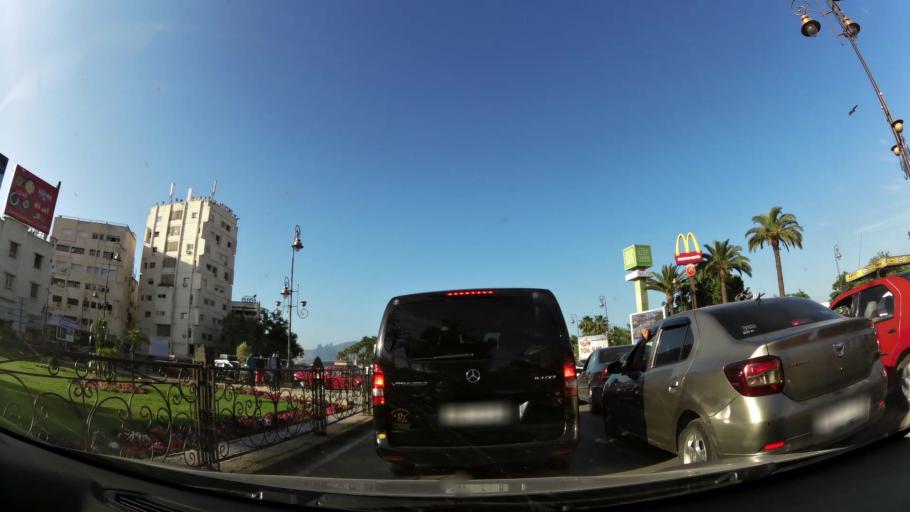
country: MA
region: Fes-Boulemane
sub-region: Fes
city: Fes
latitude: 34.0443
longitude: -4.9971
